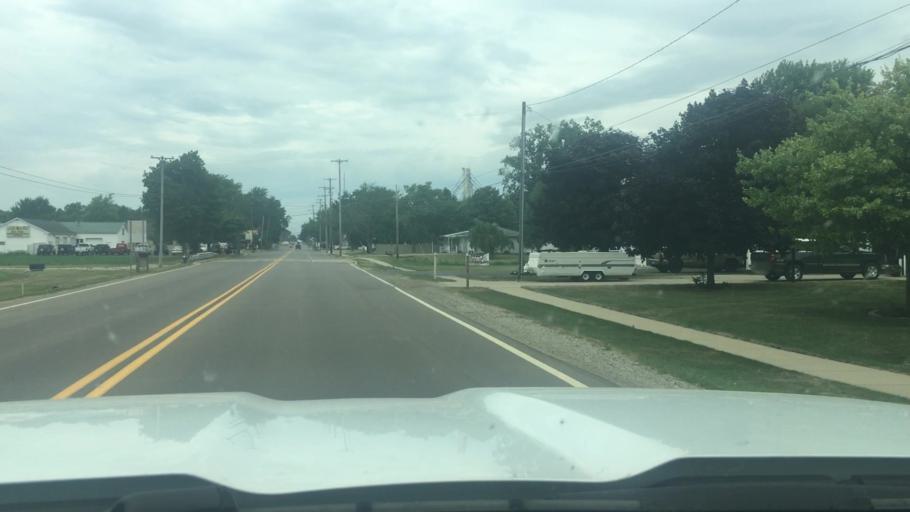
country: US
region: Michigan
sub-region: Clinton County
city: Fowler
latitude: 43.0019
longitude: -84.7323
